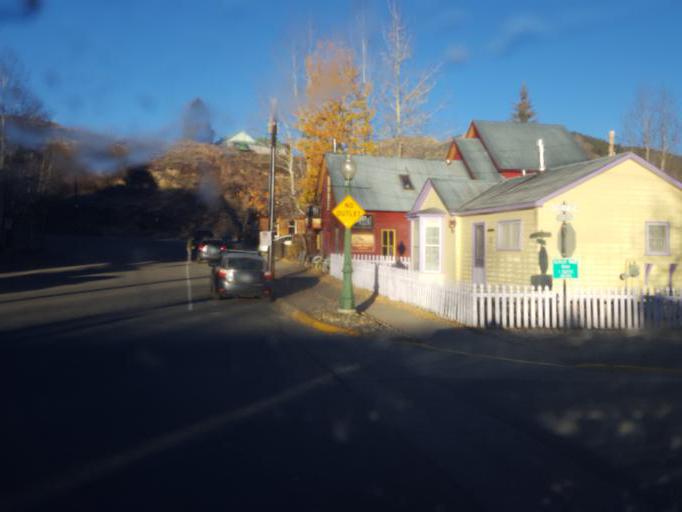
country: US
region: Colorado
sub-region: Gunnison County
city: Crested Butte
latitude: 38.8698
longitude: -106.9889
